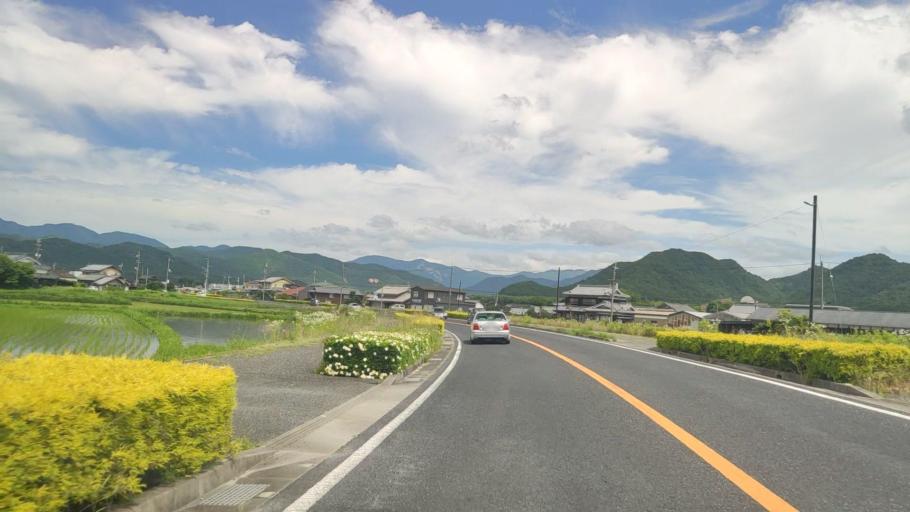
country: JP
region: Hyogo
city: Nishiwaki
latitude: 35.0324
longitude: 134.9407
